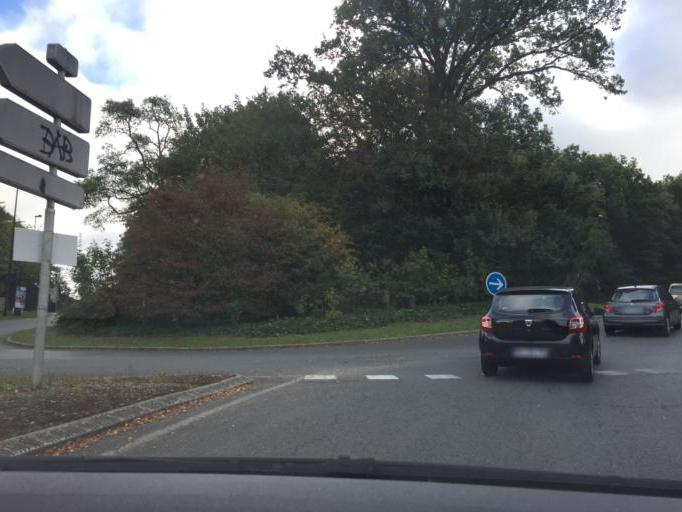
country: FR
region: Ile-de-France
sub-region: Departement de l'Essonne
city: Bures-sur-Yvette
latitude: 48.6944
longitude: 2.1648
